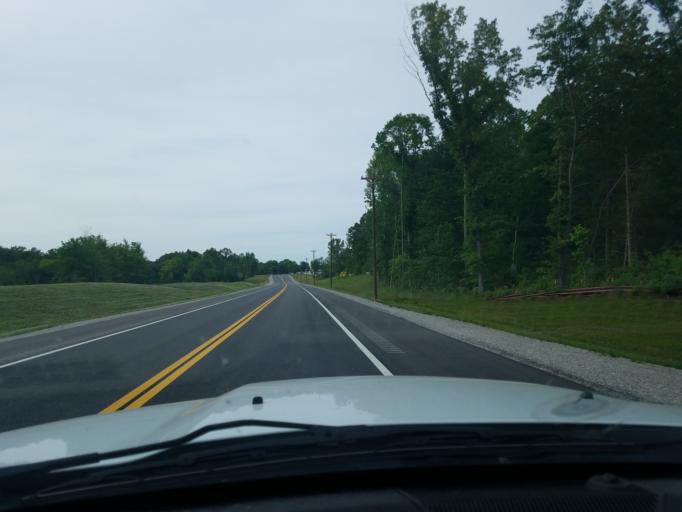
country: US
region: Tennessee
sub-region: Putnam County
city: Cookeville
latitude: 36.1715
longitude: -85.5618
